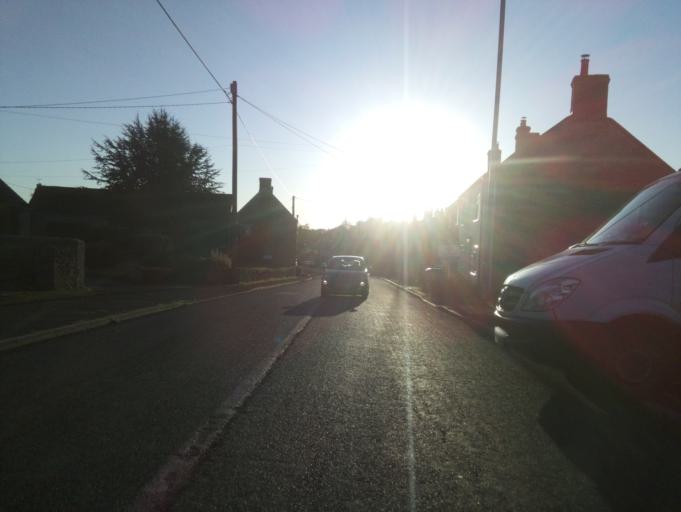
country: GB
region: England
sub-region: Somerset
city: Wincanton
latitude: 51.0614
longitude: -2.3904
